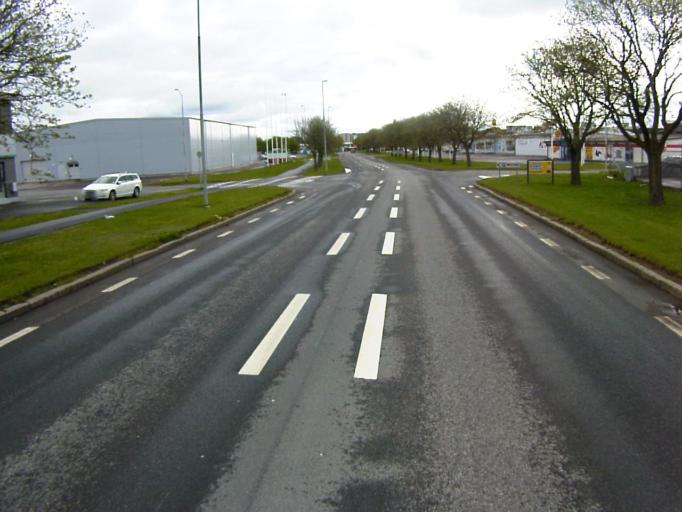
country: SE
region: Skane
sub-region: Kristianstads Kommun
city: Kristianstad
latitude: 56.0228
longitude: 14.1380
